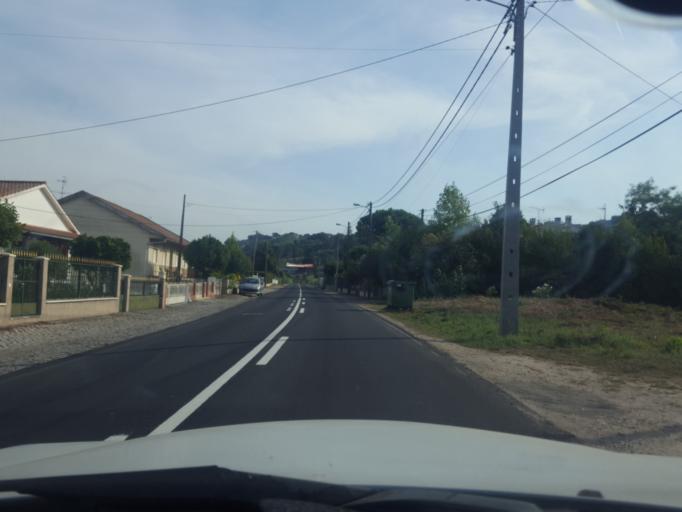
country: PT
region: Leiria
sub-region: Leiria
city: Leiria
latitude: 39.7083
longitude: -8.7929
